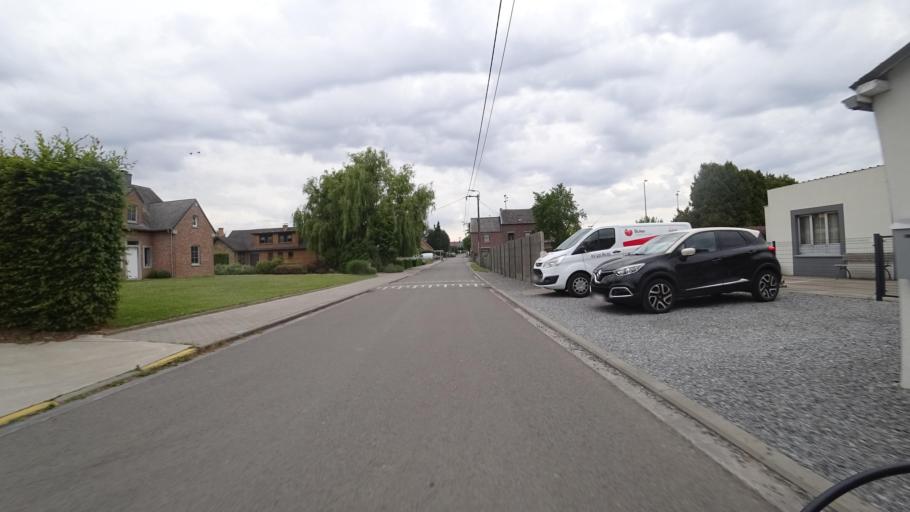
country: BE
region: Wallonia
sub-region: Province du Brabant Wallon
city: Perwez
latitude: 50.5520
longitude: 4.7963
